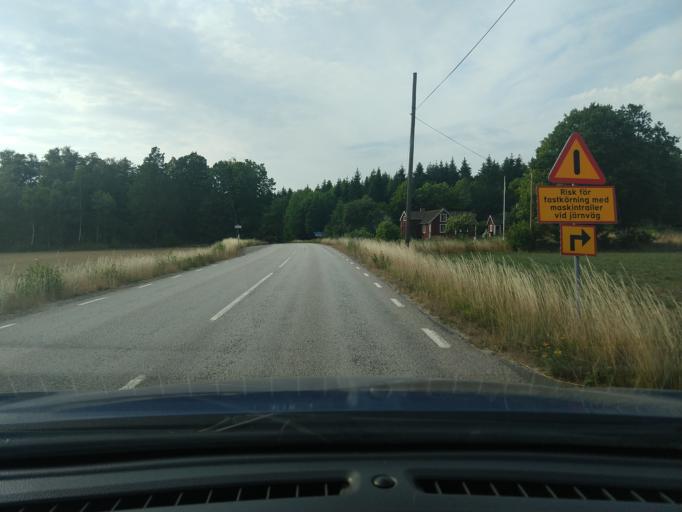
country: SE
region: Blekinge
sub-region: Ronneby Kommun
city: Kallinge
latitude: 56.2465
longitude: 15.2152
